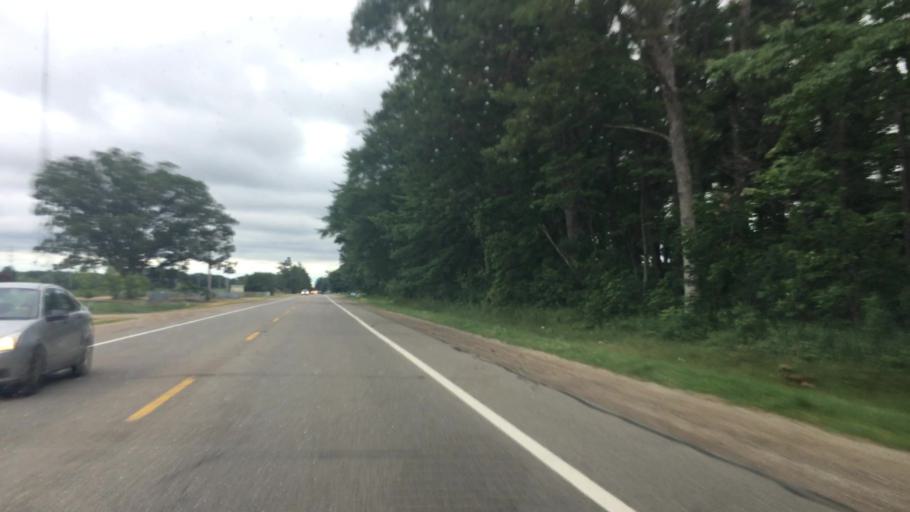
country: US
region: Michigan
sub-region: Ottawa County
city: Allendale
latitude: 42.9719
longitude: -86.0562
